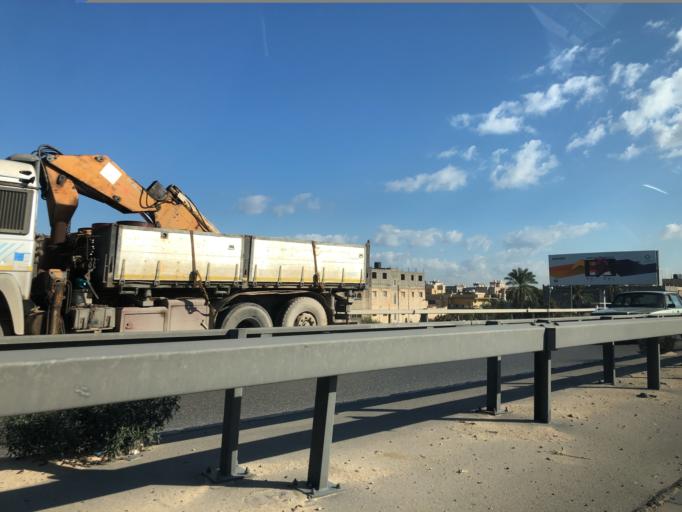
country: LY
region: Tripoli
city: Tripoli
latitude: 32.8561
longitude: 13.2012
